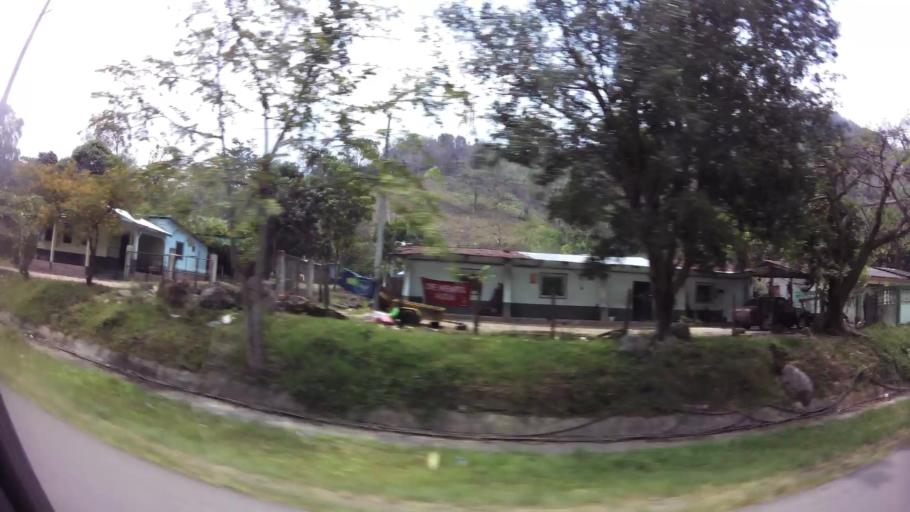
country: HN
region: Comayagua
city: Taulabe
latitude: 14.7453
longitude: -87.9610
